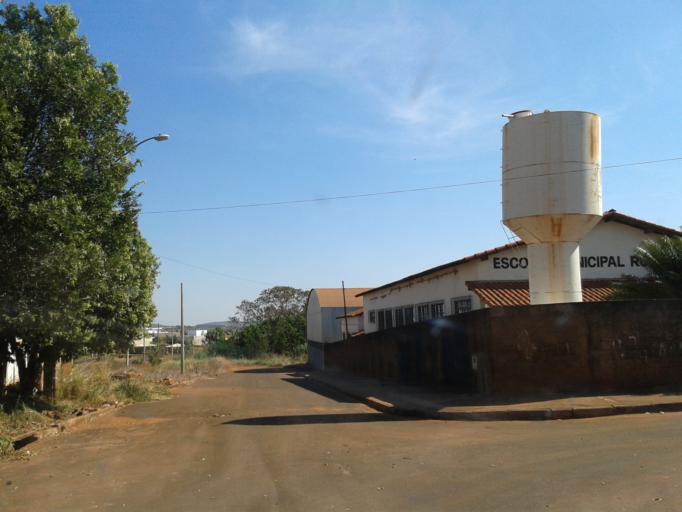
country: BR
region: Minas Gerais
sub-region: Ituiutaba
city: Ituiutaba
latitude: -19.0004
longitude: -49.4576
